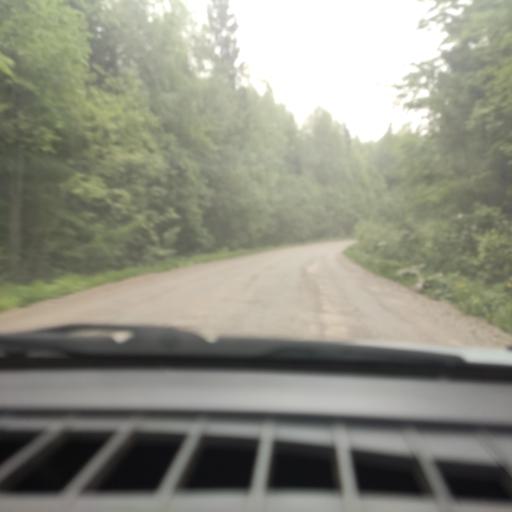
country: RU
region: Perm
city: Novyye Lyady
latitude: 57.9021
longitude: 56.6523
